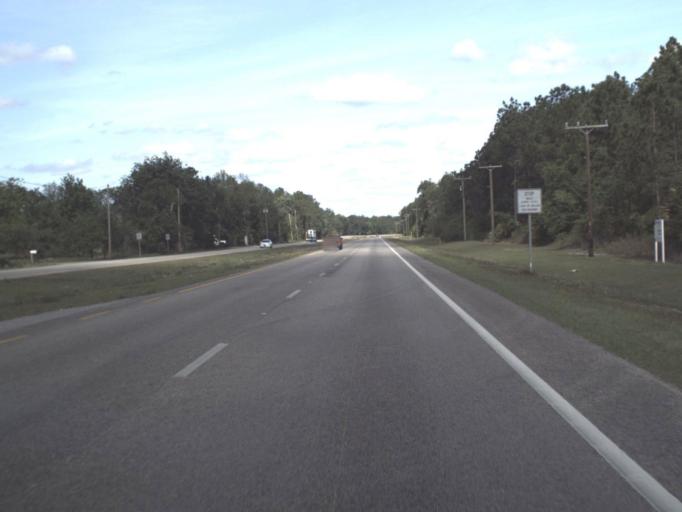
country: US
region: Florida
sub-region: Flagler County
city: Bunnell
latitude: 29.4282
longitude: -81.2245
